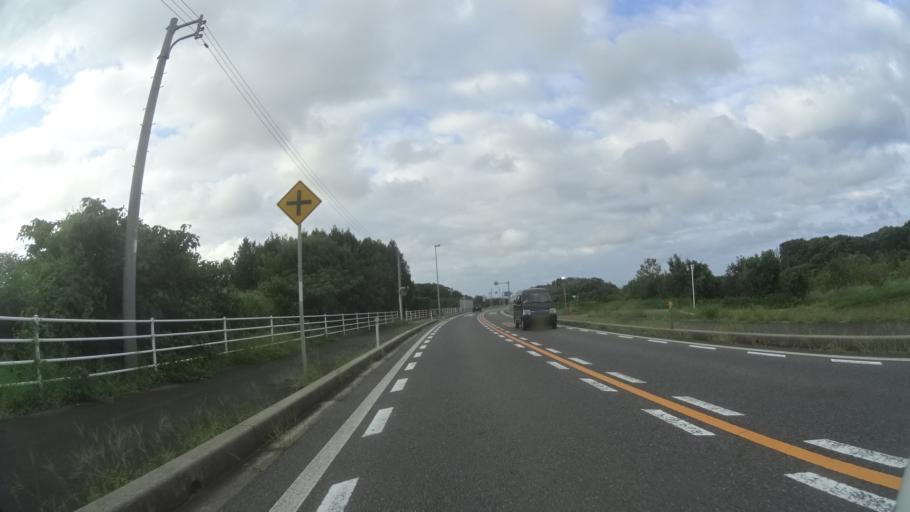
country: JP
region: Tottori
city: Kurayoshi
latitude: 35.5170
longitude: 133.5982
